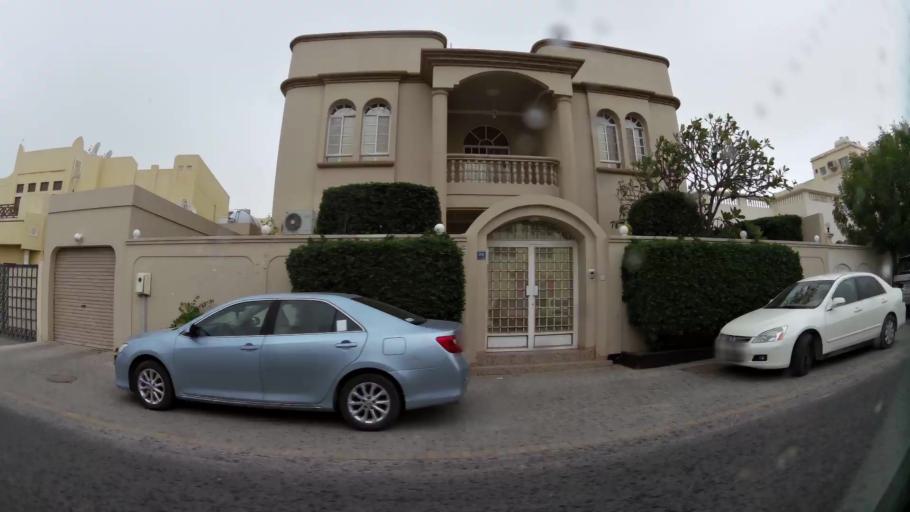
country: BH
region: Northern
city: Madinat `Isa
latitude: 26.1598
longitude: 50.5667
